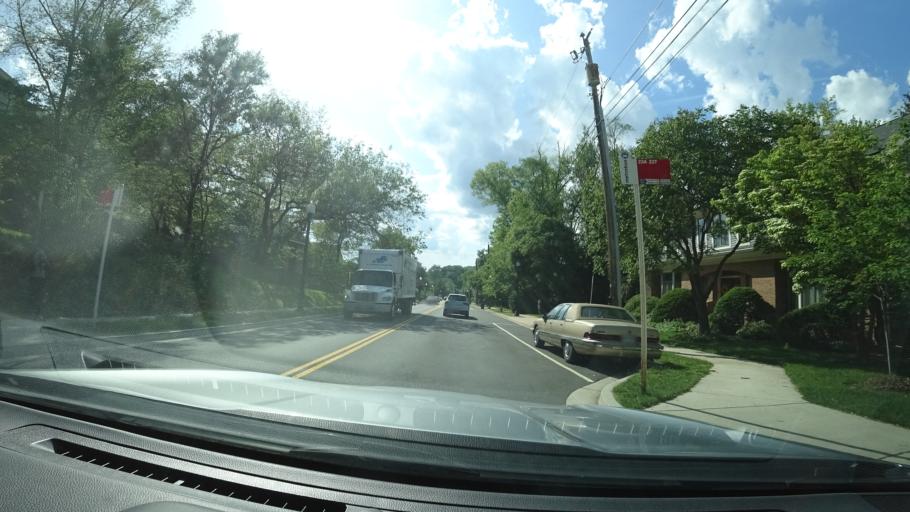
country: US
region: Maryland
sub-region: Montgomery County
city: Brookmont
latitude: 38.9098
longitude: -77.1370
